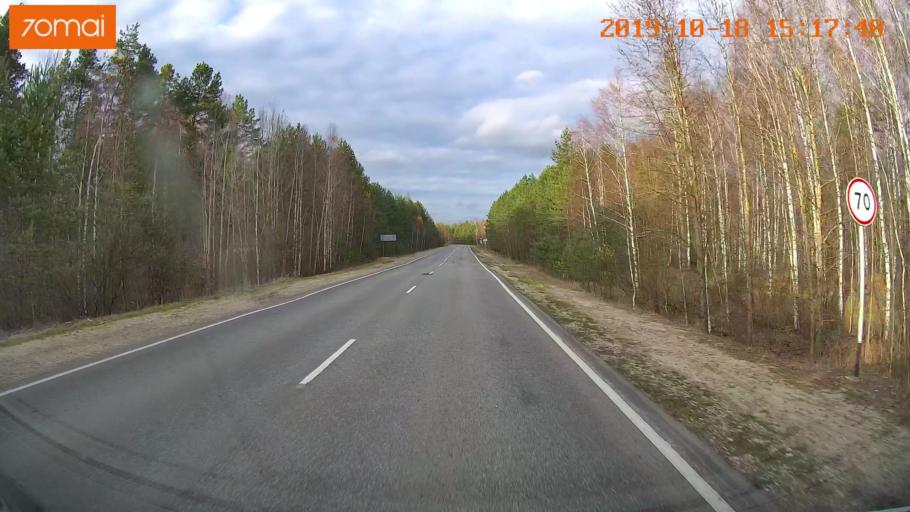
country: RU
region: Vladimir
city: Anopino
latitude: 55.6532
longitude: 40.7270
